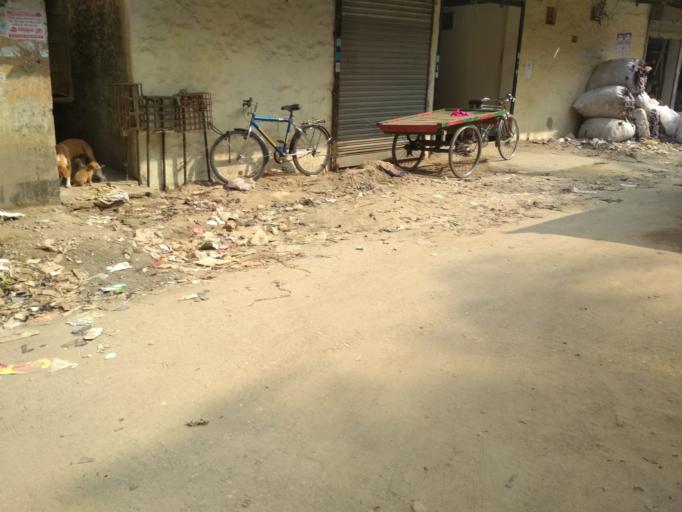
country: BD
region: Dhaka
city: Azimpur
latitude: 23.8102
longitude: 90.3737
